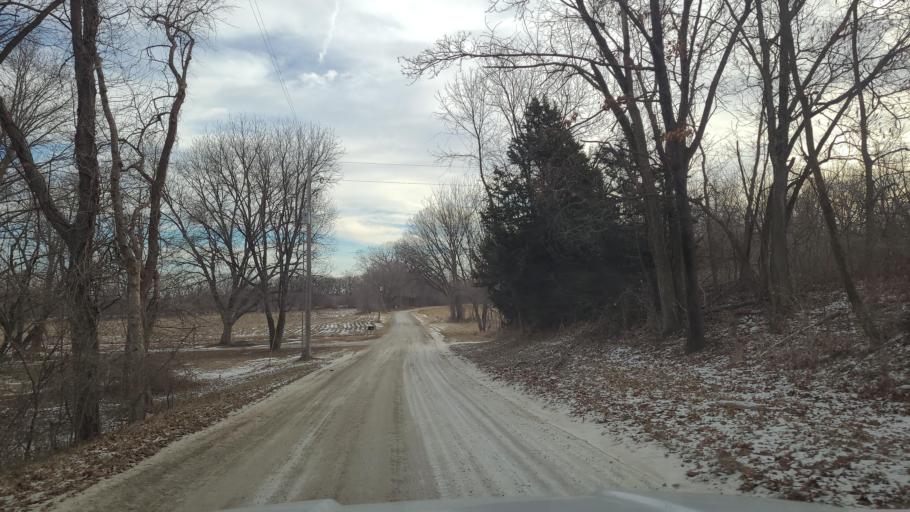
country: US
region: Kansas
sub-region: Douglas County
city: Lawrence
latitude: 39.0369
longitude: -95.3720
